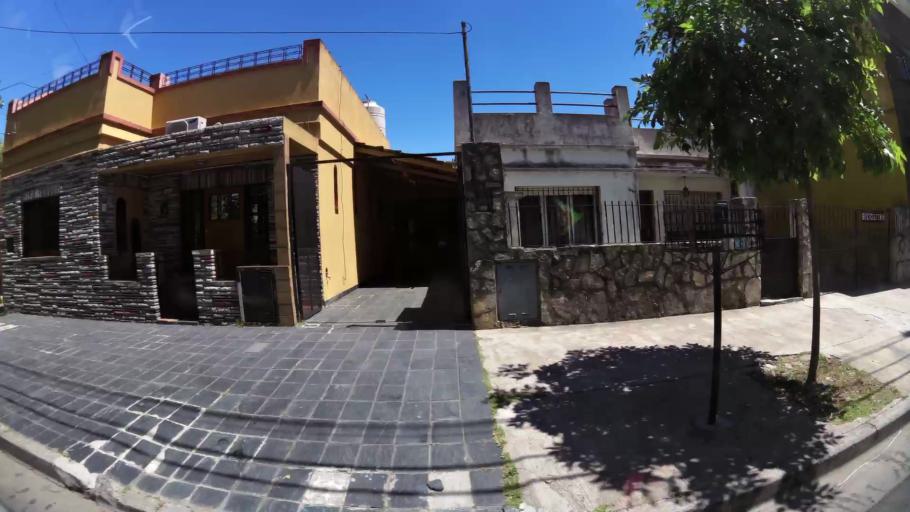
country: AR
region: Buenos Aires
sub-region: Partido de San Isidro
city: San Isidro
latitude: -34.5052
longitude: -58.5506
